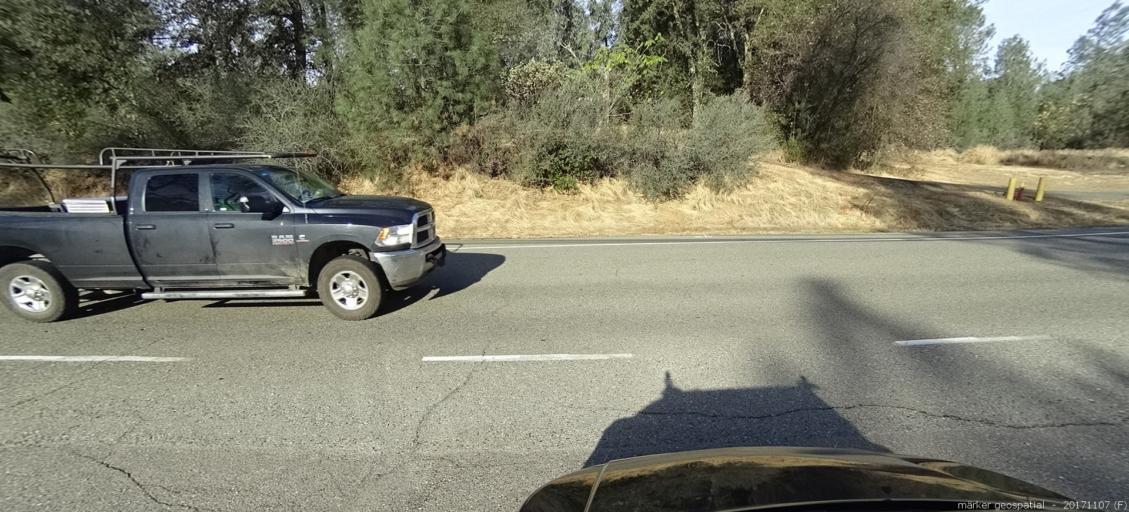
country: US
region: California
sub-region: Shasta County
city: Shasta
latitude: 40.5508
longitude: -122.4536
